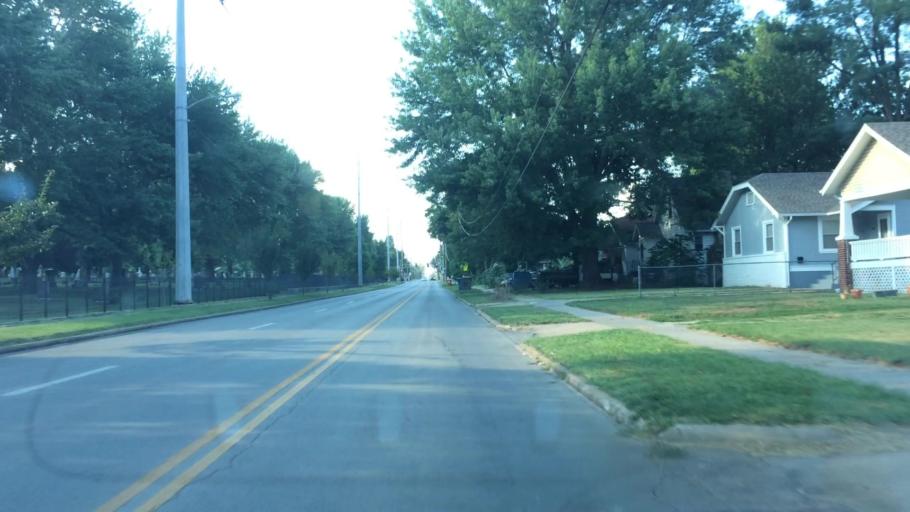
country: US
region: Missouri
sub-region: Greene County
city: Springfield
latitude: 37.1942
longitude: -93.2902
